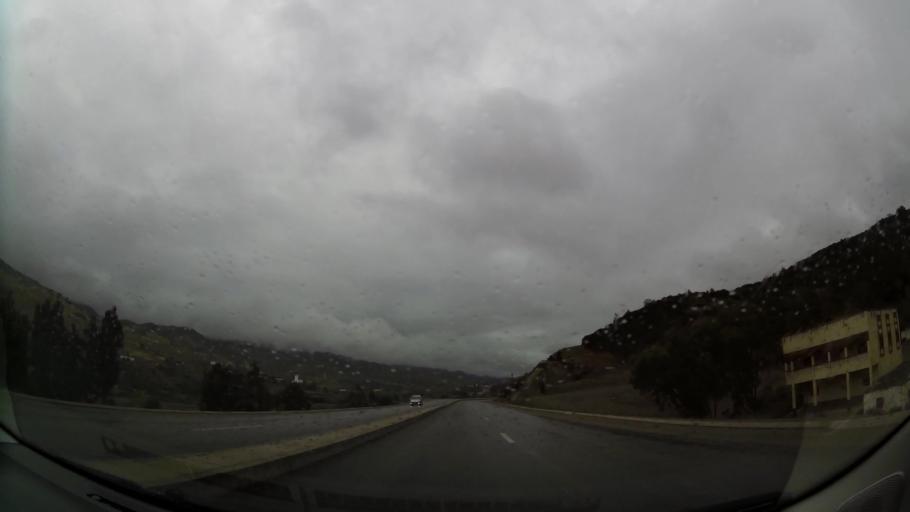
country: MA
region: Taza-Al Hoceima-Taounate
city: Imzourene
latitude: 35.0009
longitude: -3.8122
